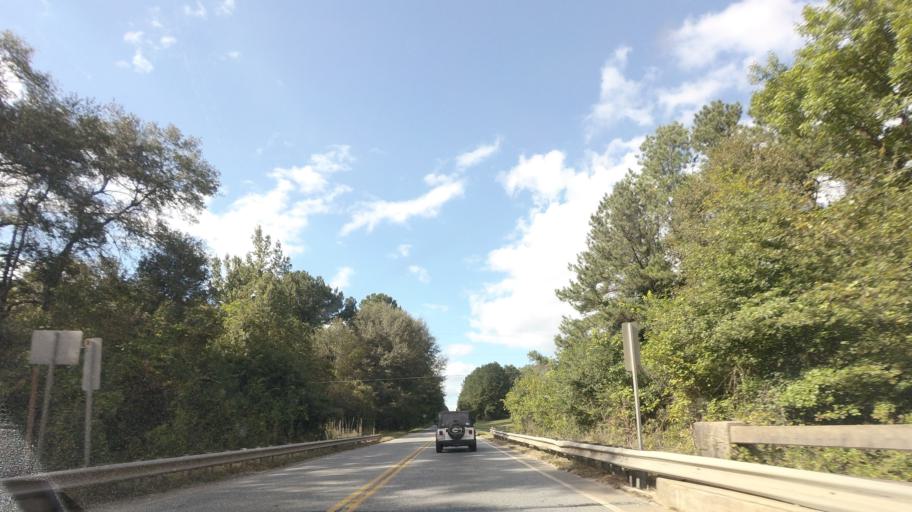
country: US
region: Georgia
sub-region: Bibb County
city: Macon
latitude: 32.9774
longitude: -83.7302
